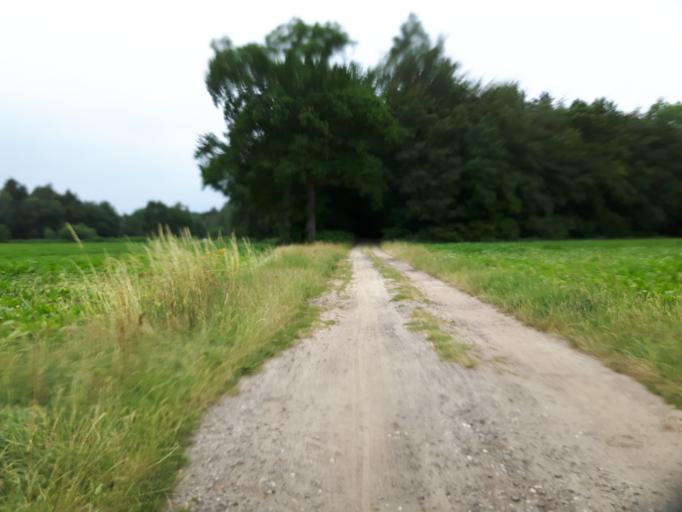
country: DE
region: Lower Saxony
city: Vierhofen
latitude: 53.2666
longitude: 10.1877
